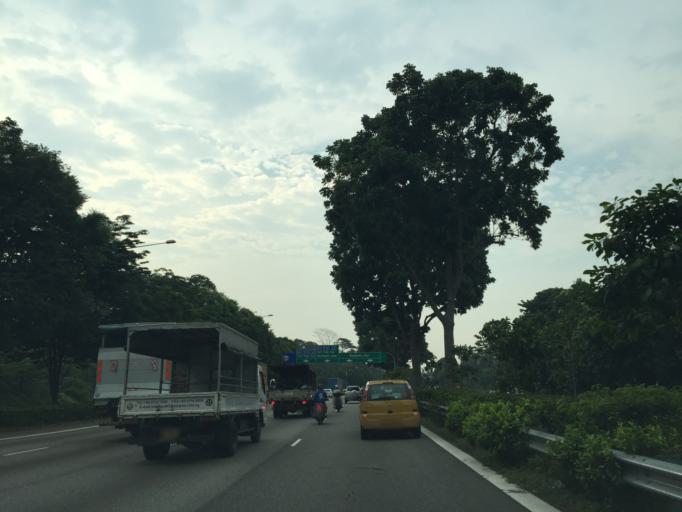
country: MY
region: Johor
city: Johor Bahru
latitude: 1.4081
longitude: 103.7720
